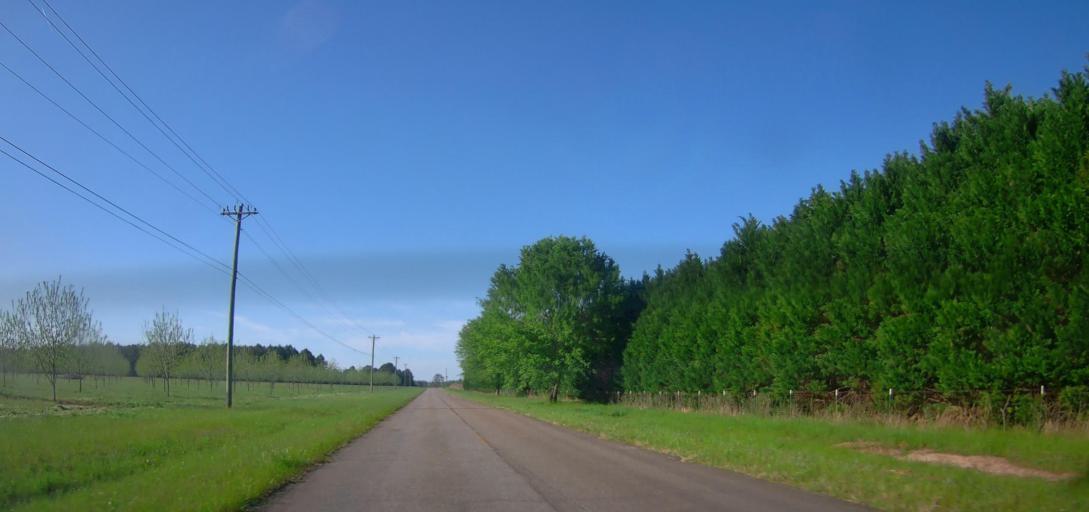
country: US
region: Georgia
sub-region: Houston County
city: Perry
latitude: 32.4462
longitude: -83.8172
